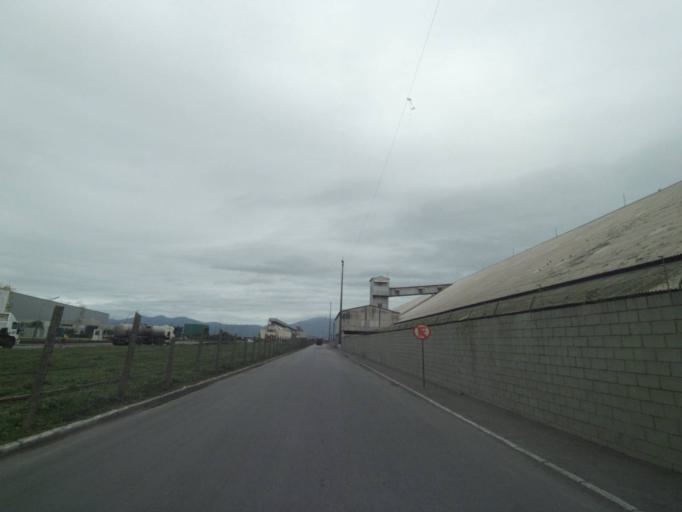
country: BR
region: Parana
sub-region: Paranagua
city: Paranagua
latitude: -25.5371
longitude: -48.5360
